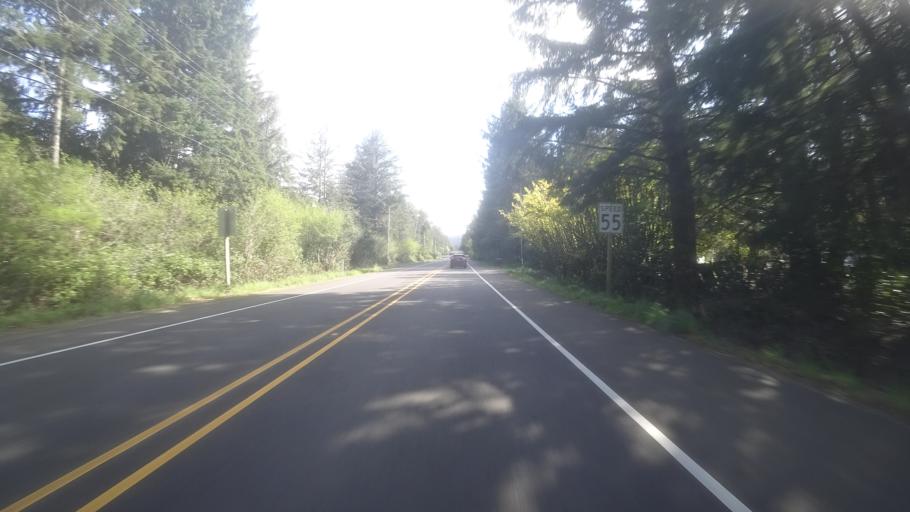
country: US
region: Oregon
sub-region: Lane County
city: Dunes City
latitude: 43.8983
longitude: -124.1170
